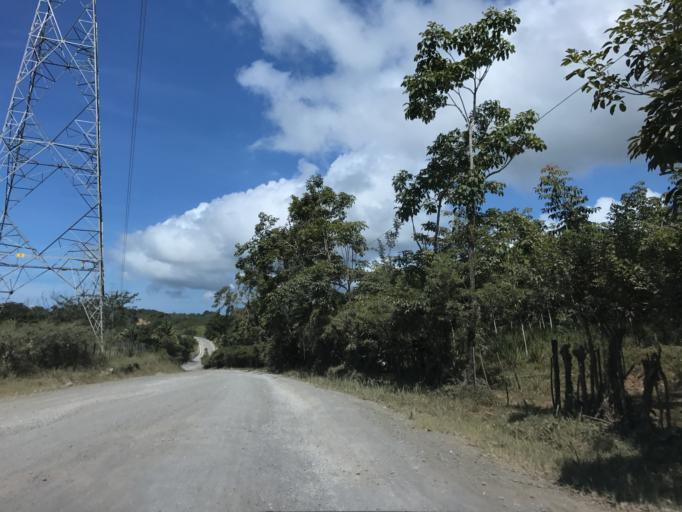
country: GT
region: Izabal
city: Morales
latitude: 15.6377
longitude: -89.0403
